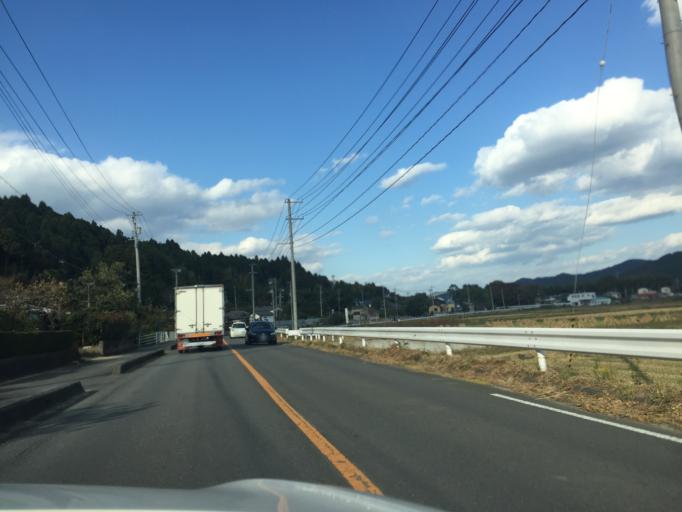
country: JP
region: Fukushima
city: Iwaki
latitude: 37.0718
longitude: 140.8707
